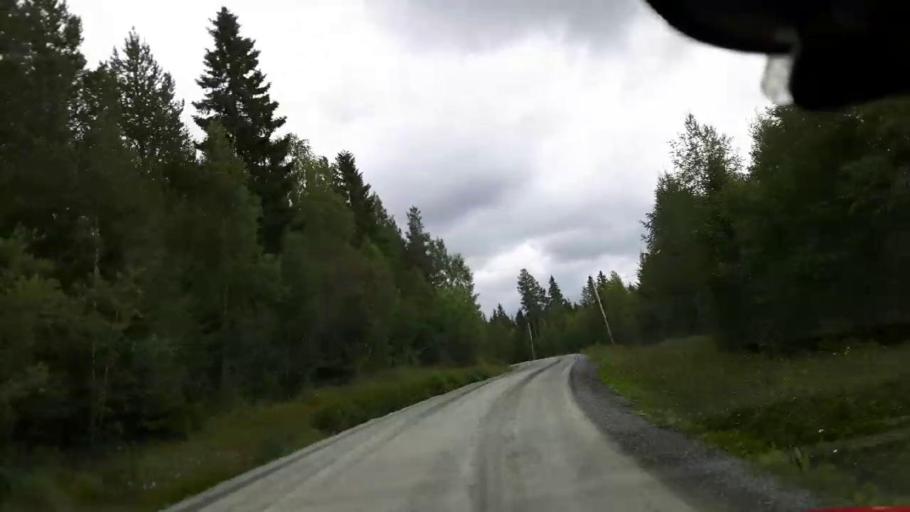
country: SE
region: Jaemtland
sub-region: Krokoms Kommun
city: Krokom
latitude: 63.5764
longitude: 14.2319
